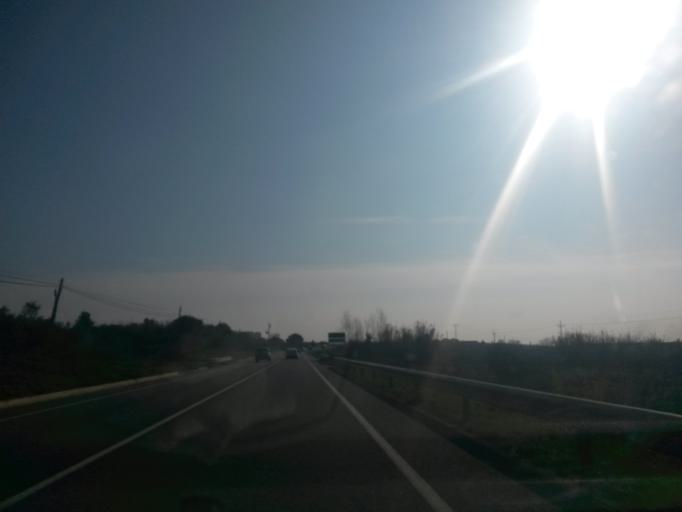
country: ES
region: Catalonia
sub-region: Provincia de Girona
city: Vilajuiga
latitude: 42.3294
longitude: 3.0872
